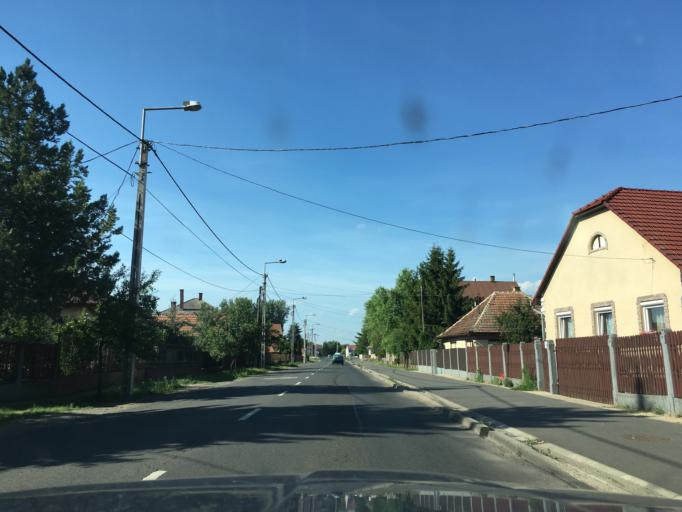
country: HU
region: Hajdu-Bihar
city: Hajdusamson
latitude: 47.6096
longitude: 21.7649
